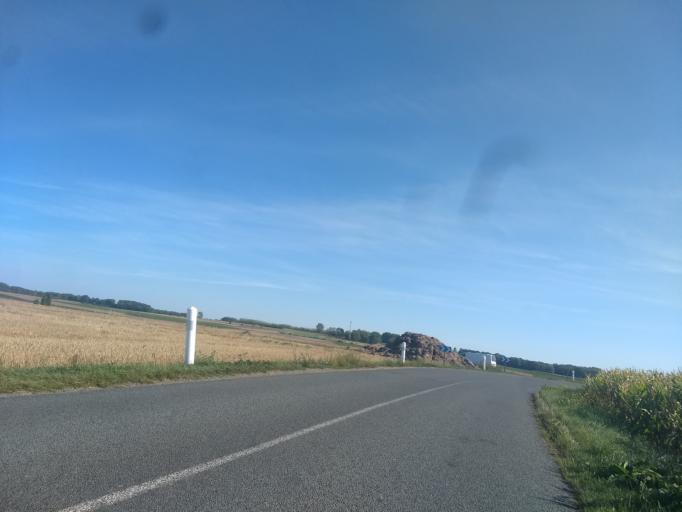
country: FR
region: Nord-Pas-de-Calais
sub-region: Departement du Pas-de-Calais
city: Roeux
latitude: 50.2851
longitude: 2.9021
